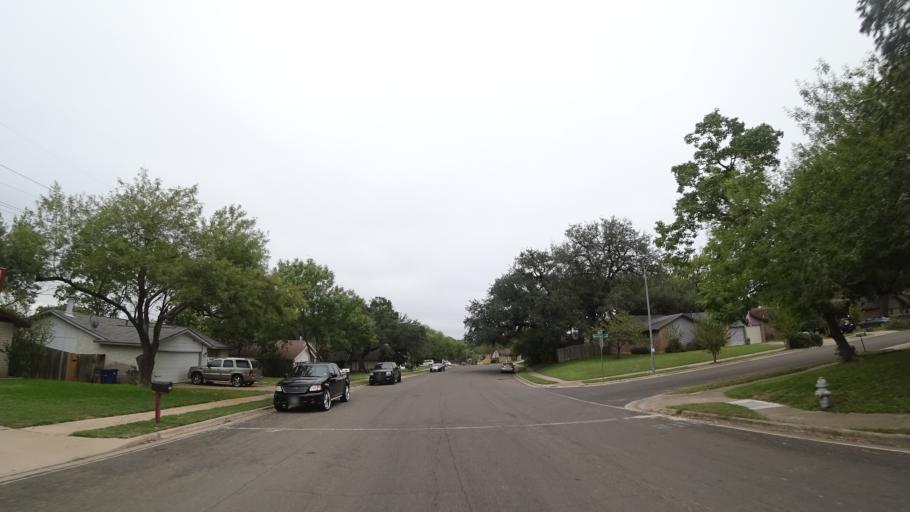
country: US
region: Texas
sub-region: Travis County
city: Onion Creek
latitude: 30.1924
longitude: -97.7821
